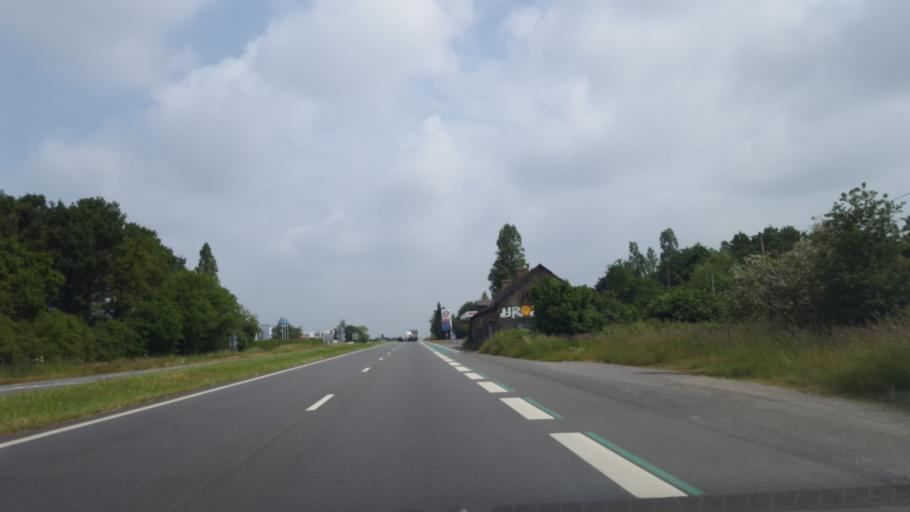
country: FR
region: Brittany
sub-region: Departement d'Ille-et-Vilaine
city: Saint-Jacques-de-la-Lande
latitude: 48.0636
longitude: -1.6990
